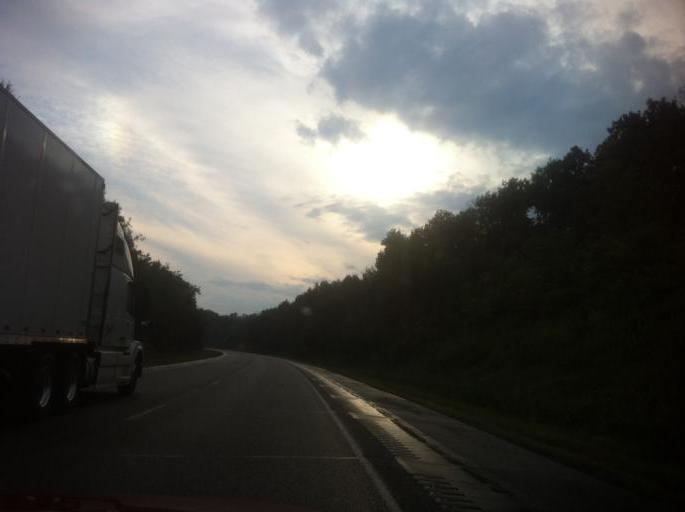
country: US
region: Pennsylvania
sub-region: Clarion County
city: Knox
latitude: 41.1984
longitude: -79.6306
